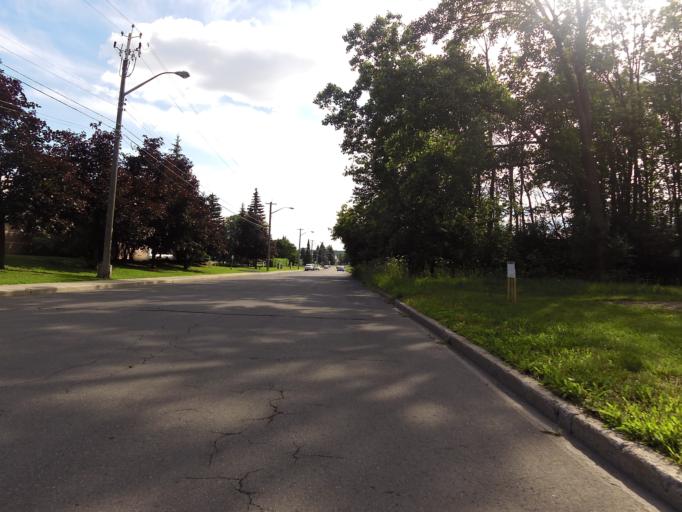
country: CA
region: Ontario
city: Bells Corners
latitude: 45.3548
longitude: -75.7838
